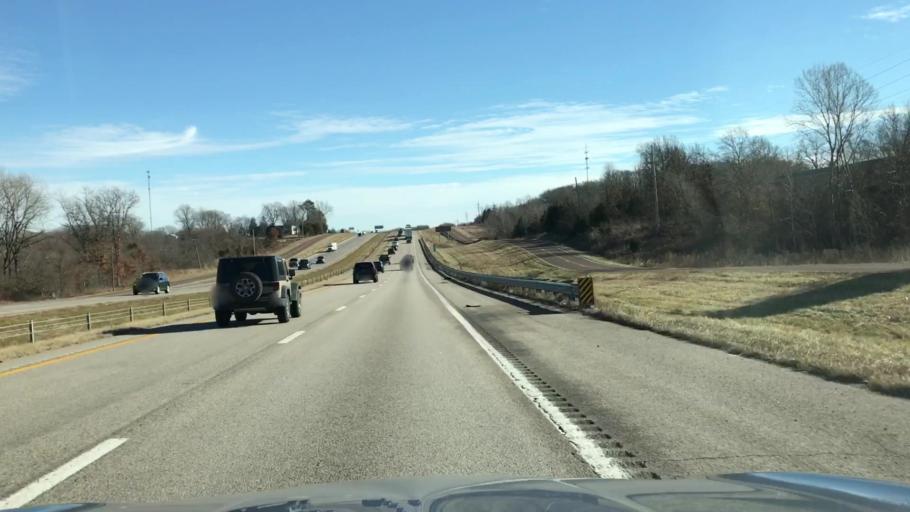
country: US
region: Missouri
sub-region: Warren County
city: Warrenton
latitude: 38.8242
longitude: -91.1991
